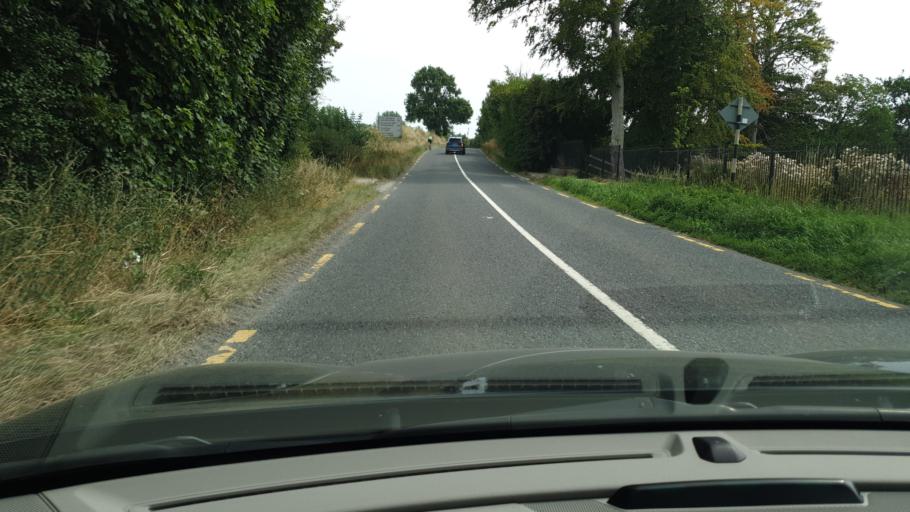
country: IE
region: Leinster
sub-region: An Mhi
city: Navan
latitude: 53.6481
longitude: -6.6514
